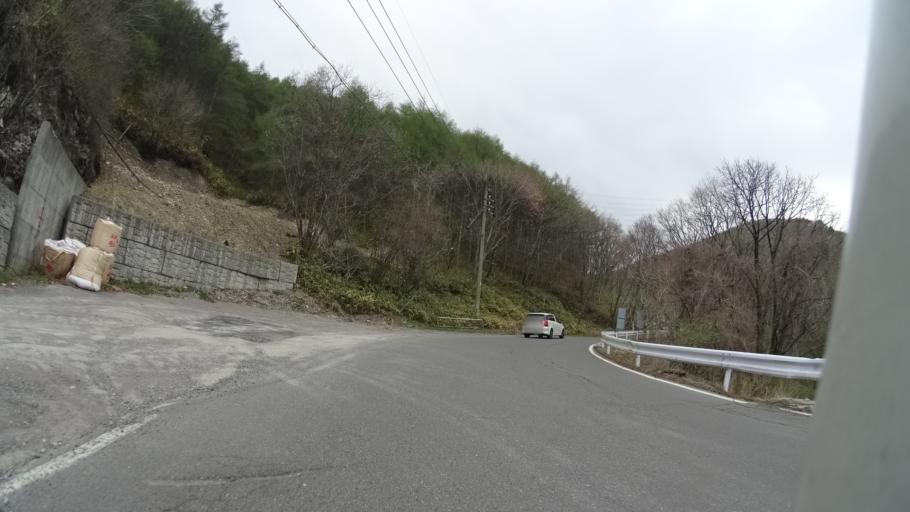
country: JP
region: Nagano
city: Suwa
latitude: 36.1396
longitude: 138.1431
